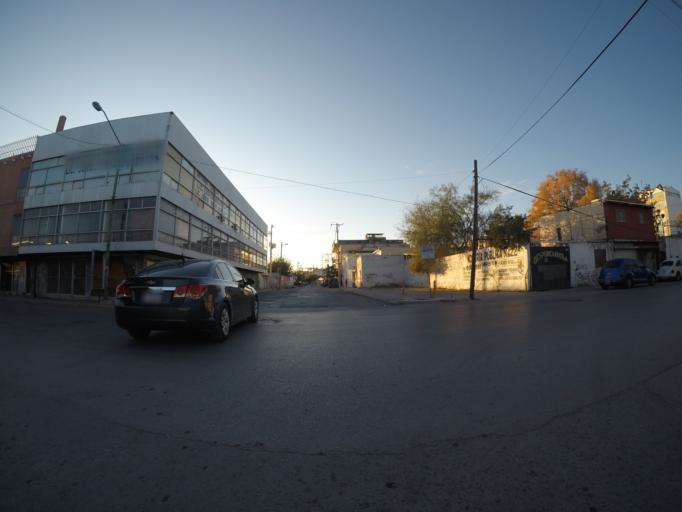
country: MX
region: Chihuahua
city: Ciudad Juarez
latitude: 31.7371
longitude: -106.4777
